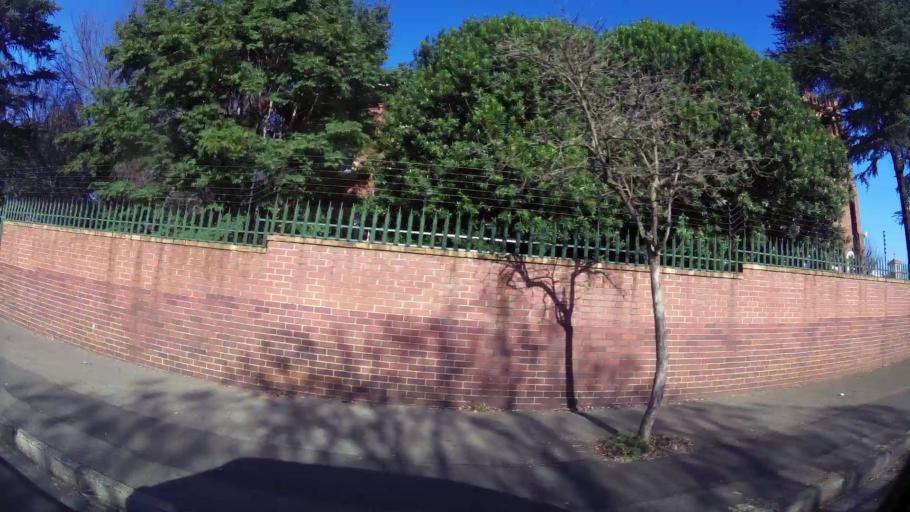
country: ZA
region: Gauteng
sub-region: Ekurhuleni Metropolitan Municipality
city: Germiston
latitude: -26.1989
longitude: 28.1228
